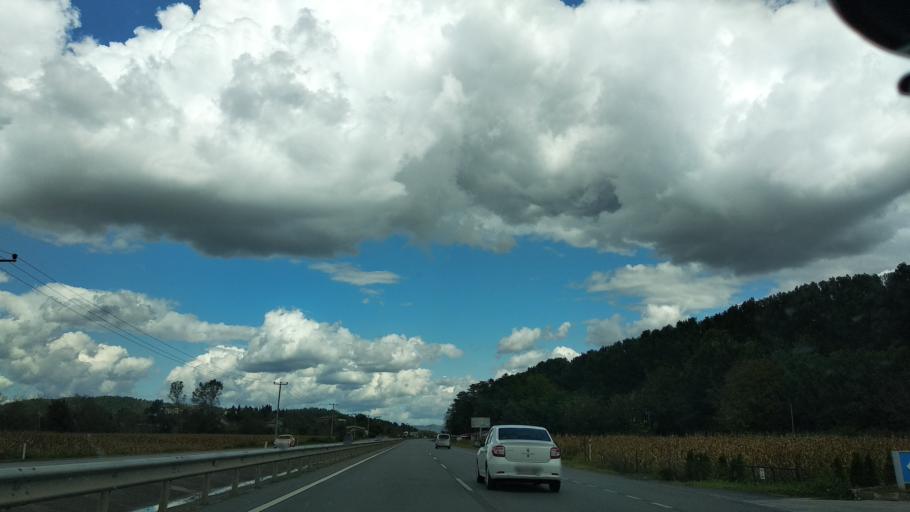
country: TR
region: Sakarya
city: Sogutlu
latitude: 40.8286
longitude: 30.4699
